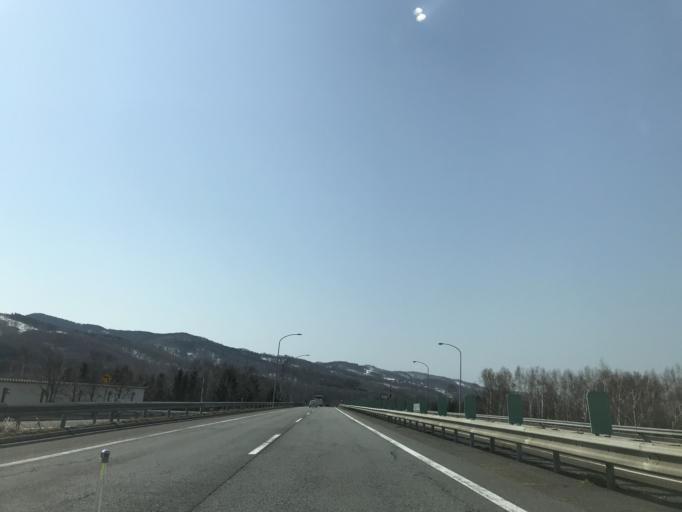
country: JP
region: Hokkaido
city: Bibai
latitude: 43.3345
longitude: 141.8882
